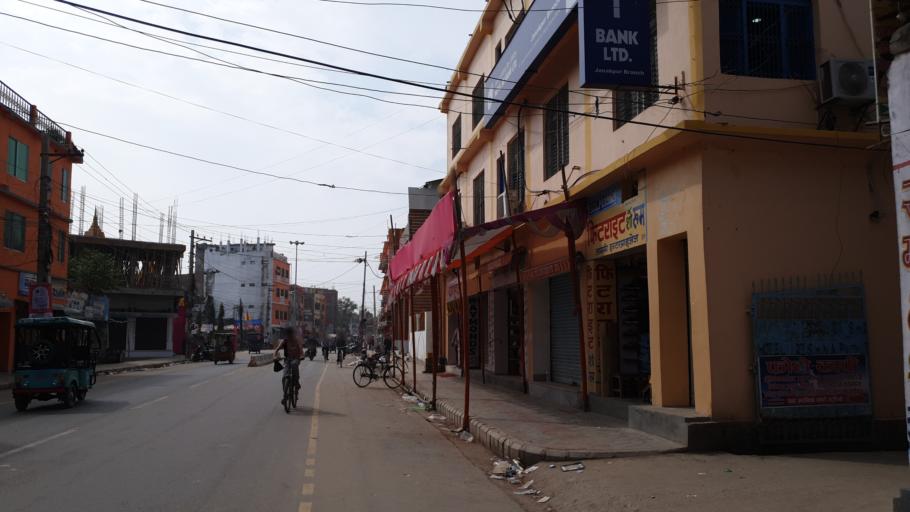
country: NP
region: Central Region
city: Janakpur
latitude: 26.7300
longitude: 85.9301
